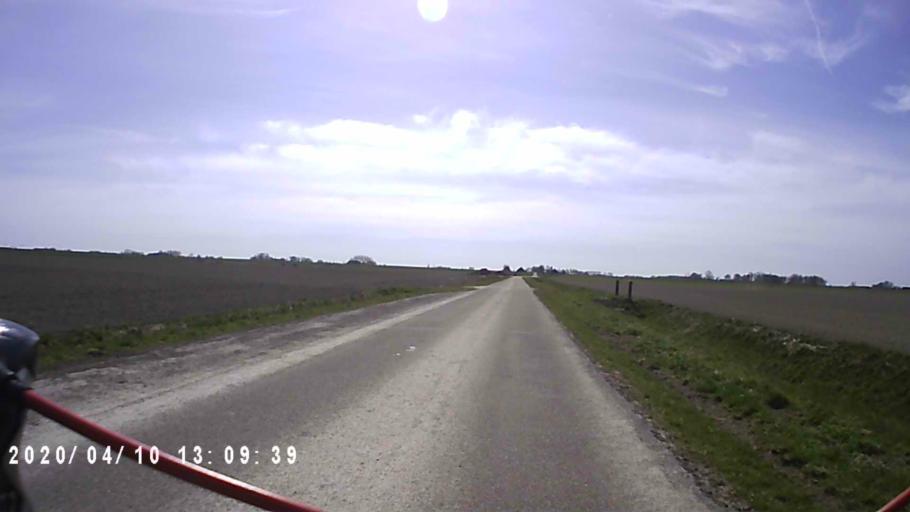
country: NL
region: Groningen
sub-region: Gemeente De Marne
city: Ulrum
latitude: 53.4127
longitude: 6.4198
